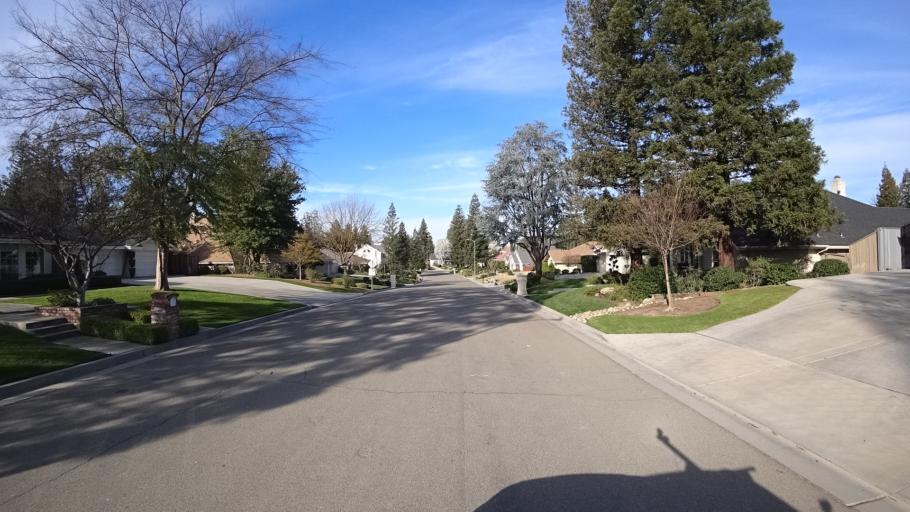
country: US
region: California
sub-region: Fresno County
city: Clovis
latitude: 36.8696
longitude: -119.7753
